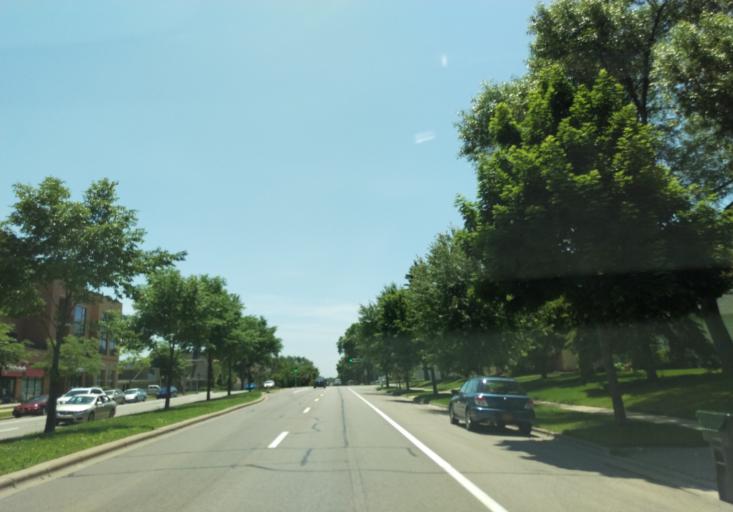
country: US
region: Wisconsin
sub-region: Dane County
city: Shorewood Hills
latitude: 43.0546
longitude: -89.4512
